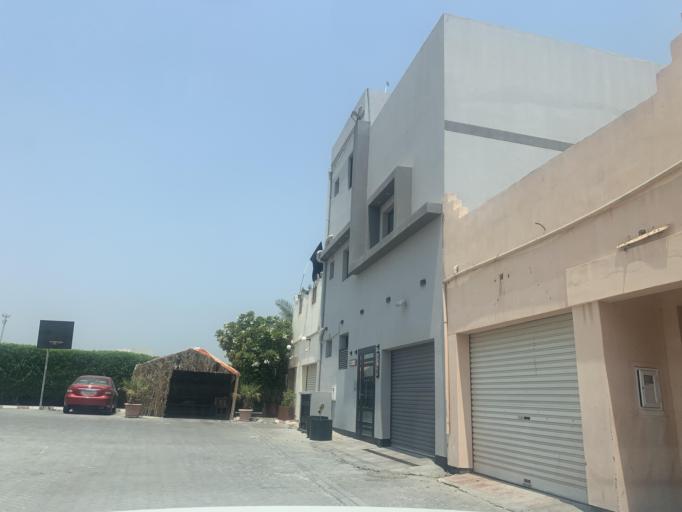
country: BH
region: Central Governorate
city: Madinat Hamad
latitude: 26.1427
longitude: 50.4646
